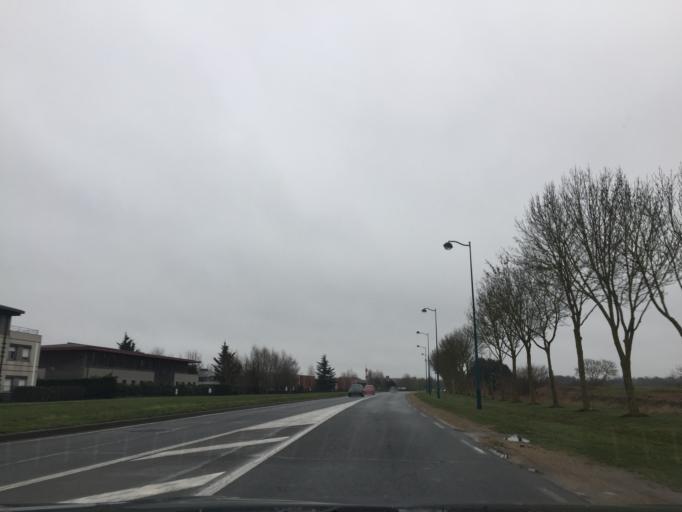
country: FR
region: Ile-de-France
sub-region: Departement de Seine-et-Marne
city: Magny-le-Hongre
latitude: 48.8663
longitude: 2.8079
